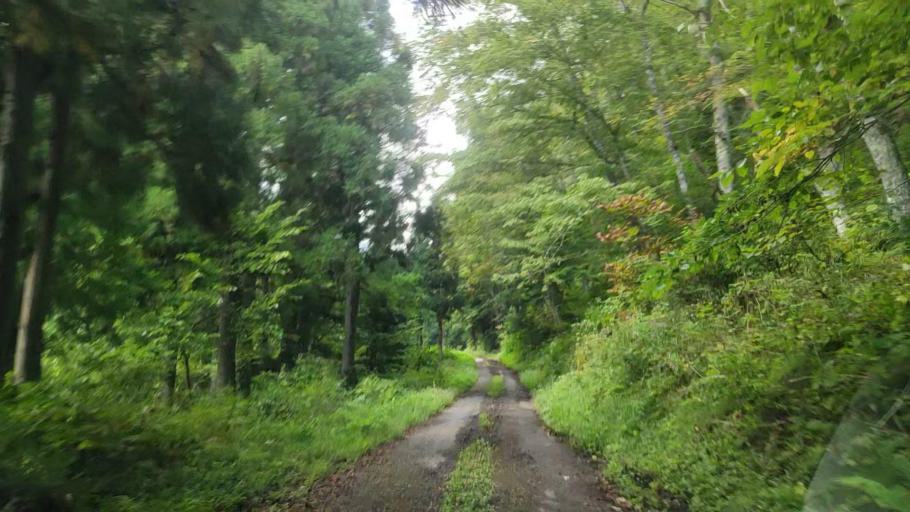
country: JP
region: Gifu
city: Takayama
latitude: 36.3165
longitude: 137.0843
